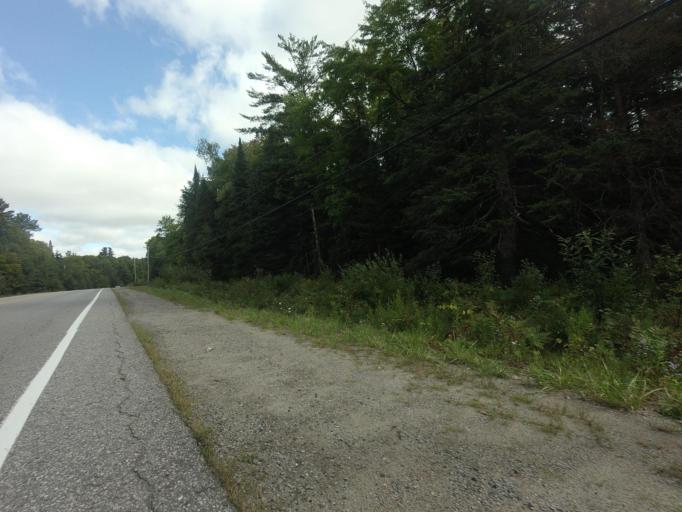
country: CA
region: Ontario
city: Omemee
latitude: 44.7968
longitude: -78.6373
